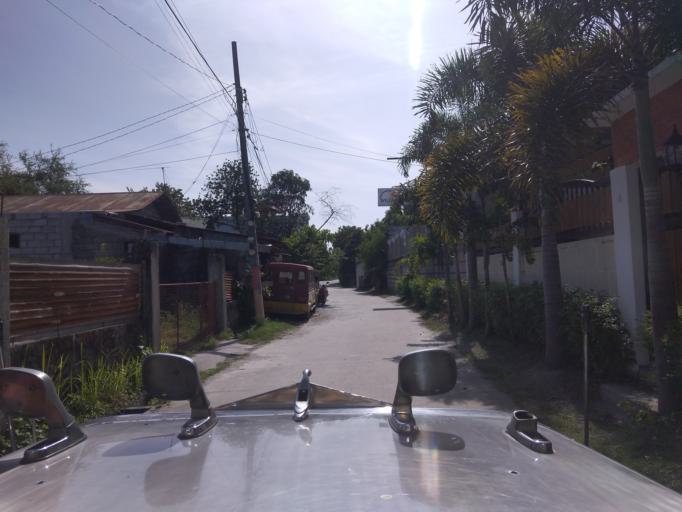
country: PH
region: Central Luzon
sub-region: Province of Pampanga
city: Bacolor
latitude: 14.9929
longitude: 120.6509
